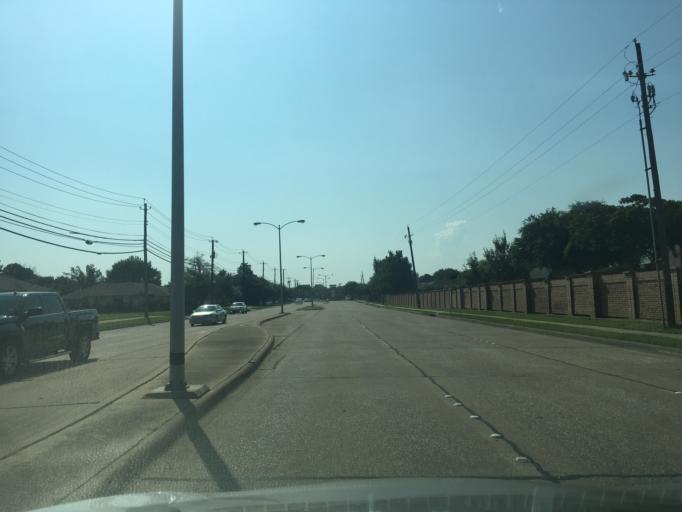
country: US
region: Texas
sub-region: Dallas County
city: Garland
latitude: 32.9428
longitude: -96.6430
